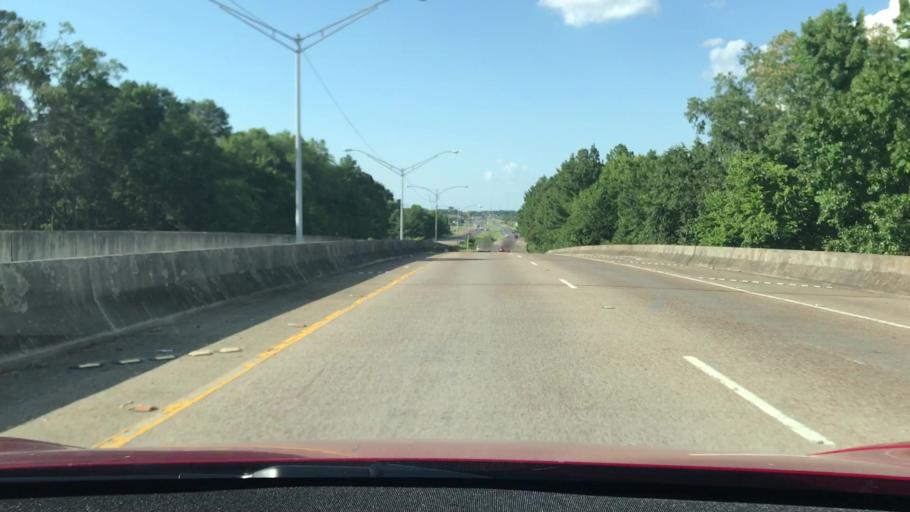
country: US
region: Louisiana
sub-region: Bossier Parish
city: Bossier City
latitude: 32.4307
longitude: -93.7844
